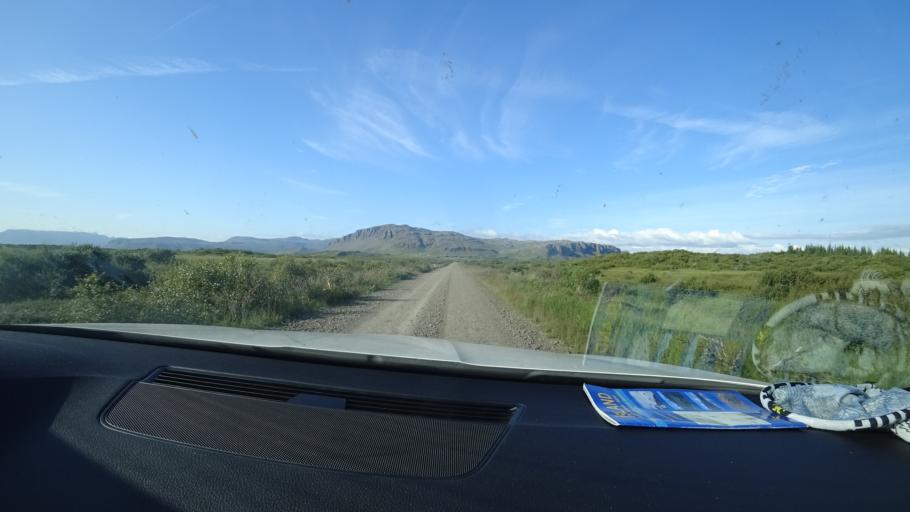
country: IS
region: West
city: Borgarnes
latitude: 64.6763
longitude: -21.9565
